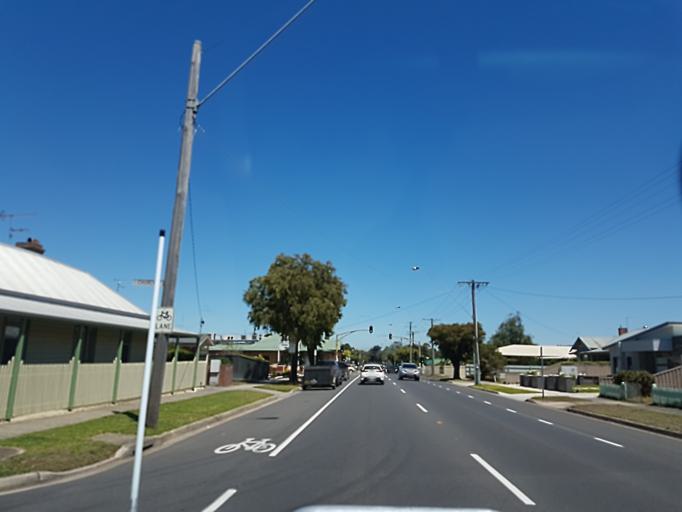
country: AU
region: Victoria
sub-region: Colac-Otway
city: Colac
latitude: -38.3372
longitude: 143.5998
